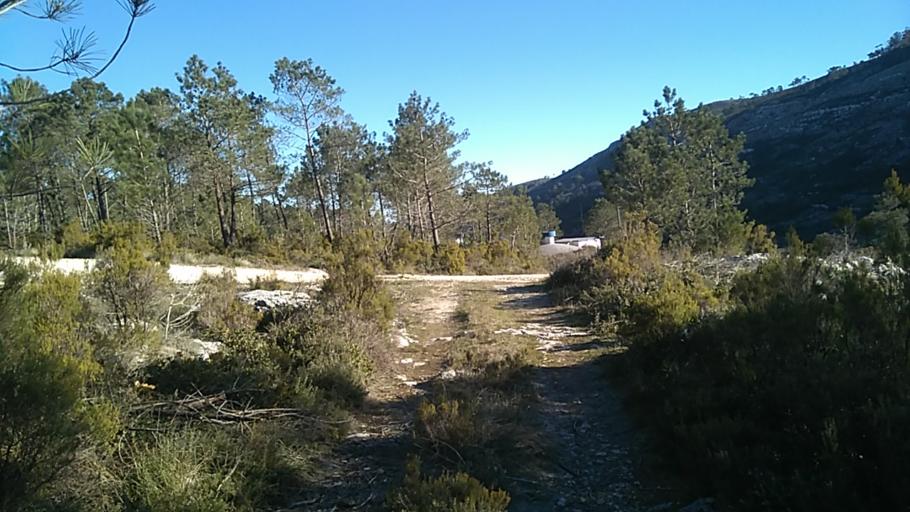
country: PT
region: Leiria
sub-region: Alcobaca
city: Aljubarrota
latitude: 39.5350
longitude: -8.8584
